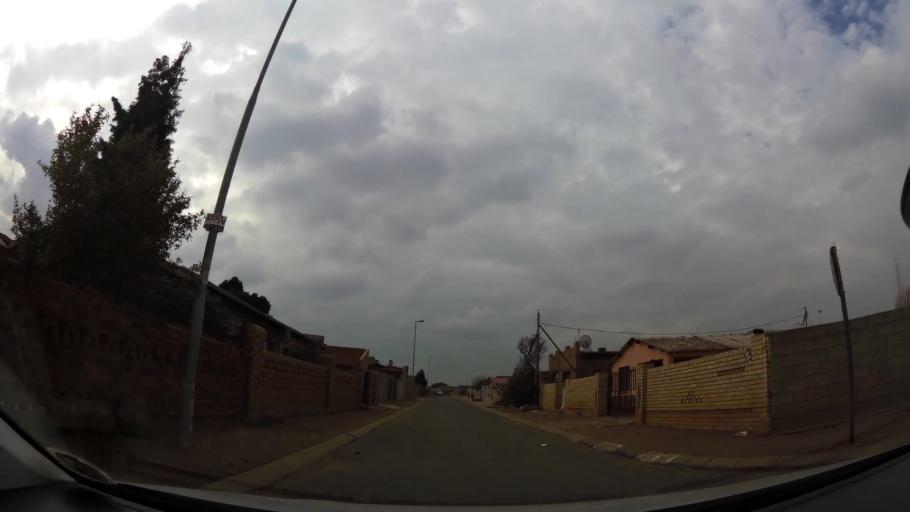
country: ZA
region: Gauteng
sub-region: City of Johannesburg Metropolitan Municipality
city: Soweto
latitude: -26.2625
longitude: 27.8532
